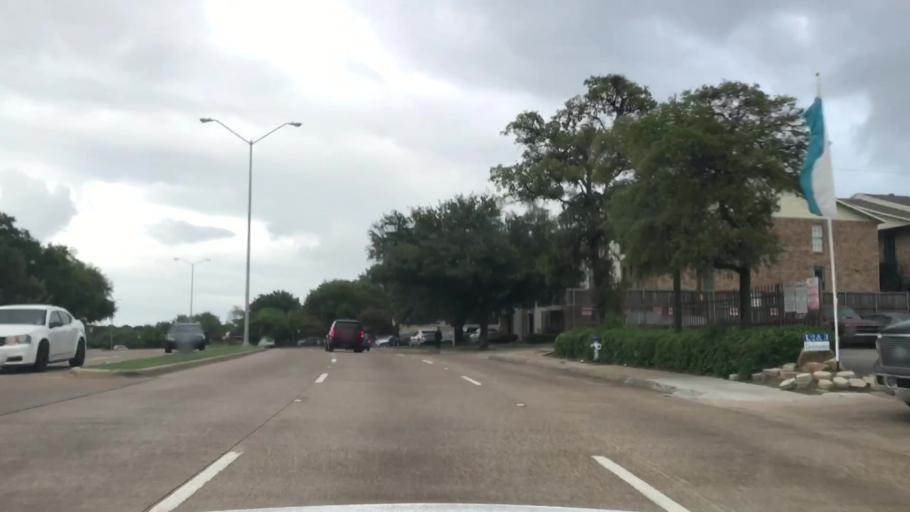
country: US
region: Texas
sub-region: Dallas County
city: Richardson
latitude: 32.8925
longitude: -96.7395
